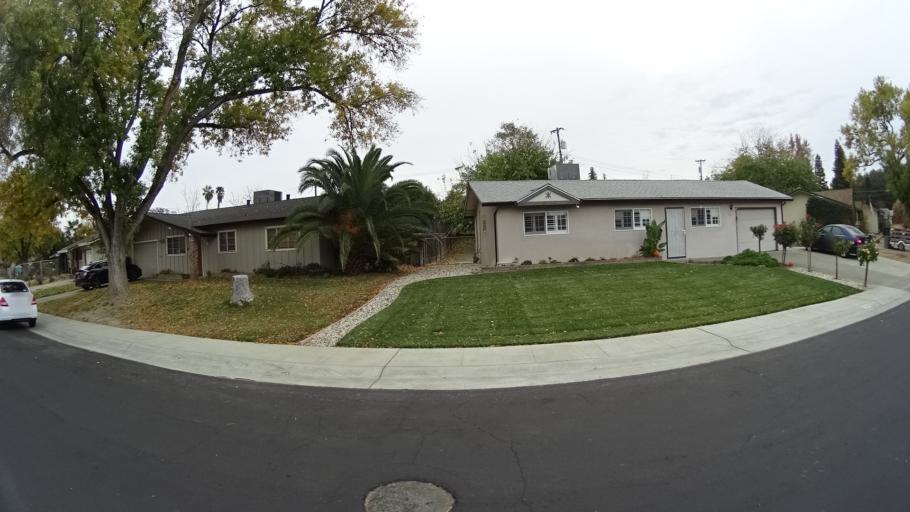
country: US
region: California
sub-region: Sacramento County
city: Citrus Heights
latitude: 38.7117
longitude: -121.2991
